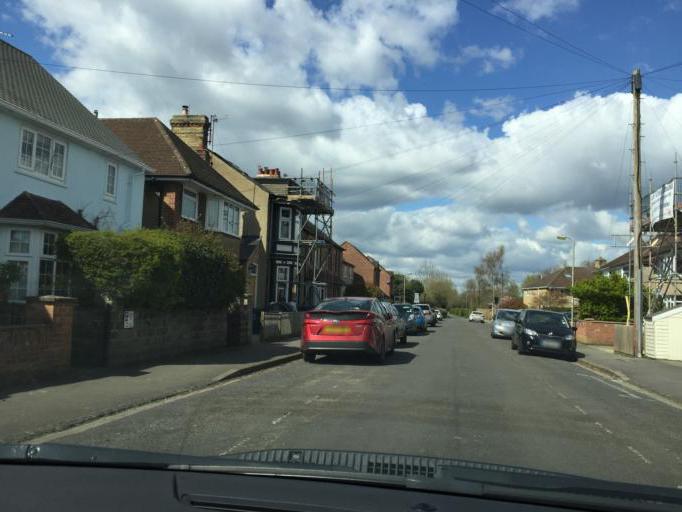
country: GB
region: England
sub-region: Oxfordshire
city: Oxford
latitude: 51.7615
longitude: -1.2399
